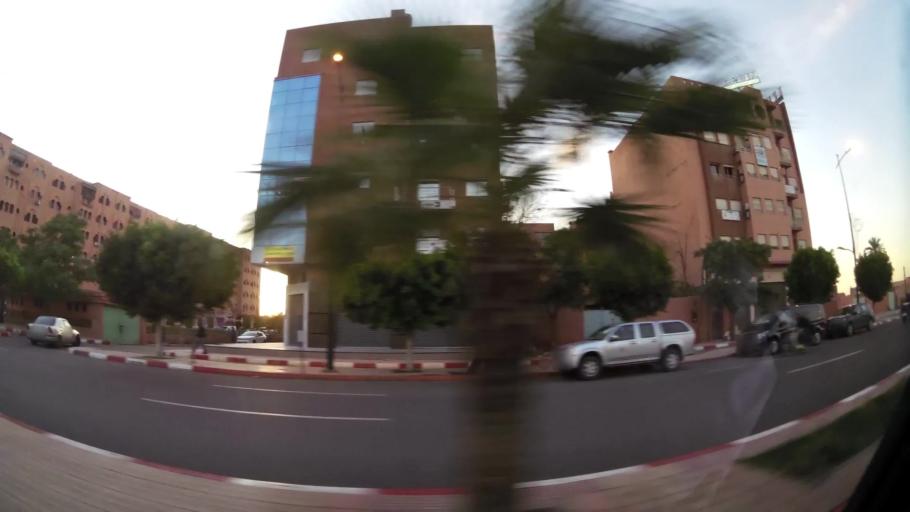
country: MA
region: Marrakech-Tensift-Al Haouz
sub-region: Marrakech
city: Marrakesh
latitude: 31.6390
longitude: -7.9983
